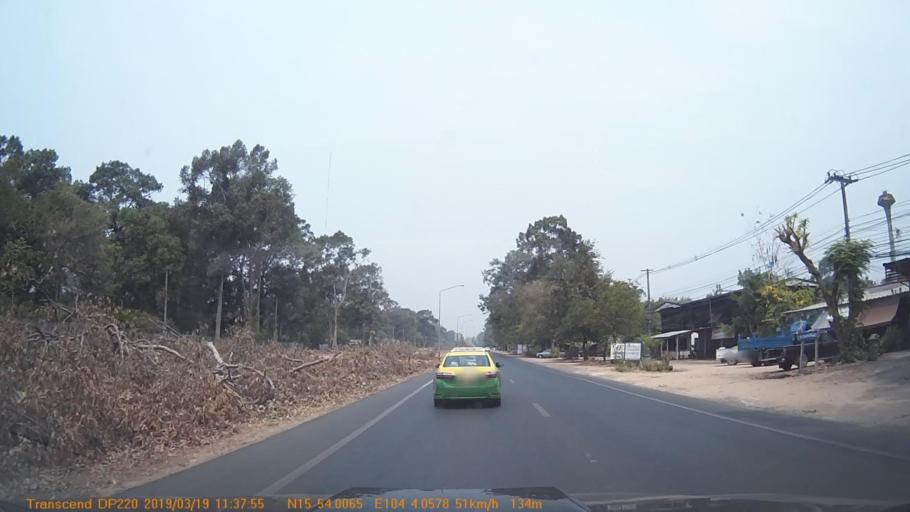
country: TH
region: Yasothon
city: Yasothon
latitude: 15.9002
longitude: 104.0676
